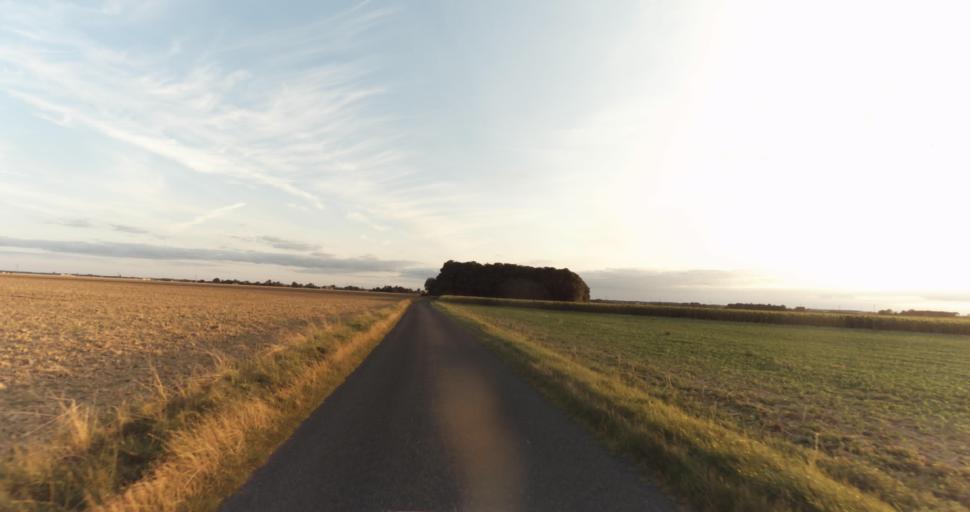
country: FR
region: Haute-Normandie
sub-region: Departement de l'Eure
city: La Madeleine-de-Nonancourt
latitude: 48.8859
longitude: 1.2084
